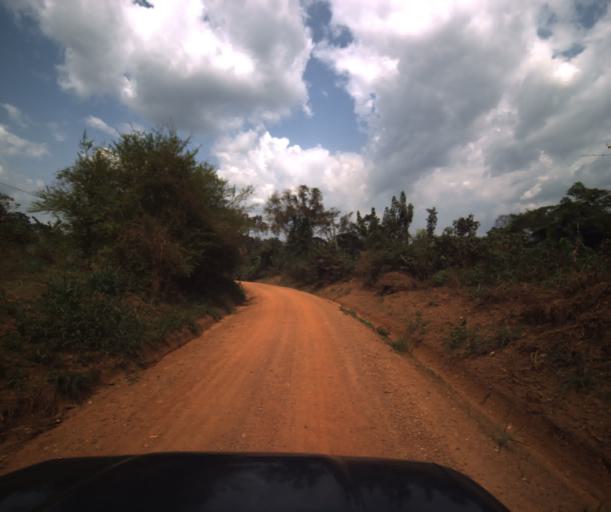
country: CM
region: Centre
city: Akono
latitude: 3.5584
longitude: 11.0776
